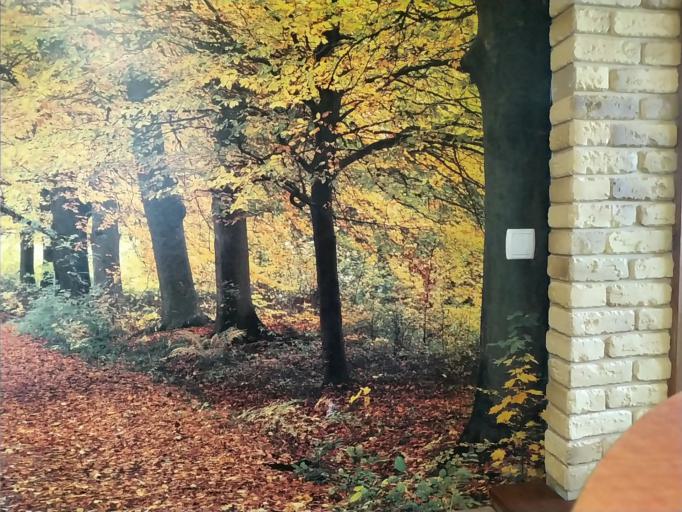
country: RU
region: Arkhangelskaya
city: Kargopol'
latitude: 60.9086
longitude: 38.8827
